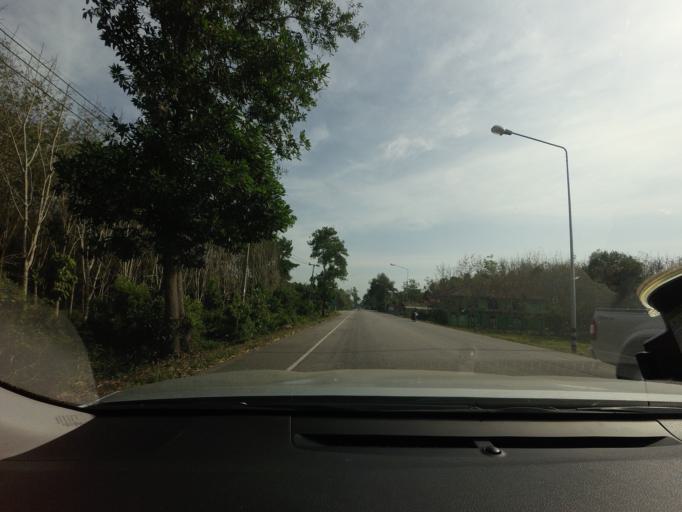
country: TH
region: Narathiwat
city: Ra-ngae
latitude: 6.3342
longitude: 101.7895
